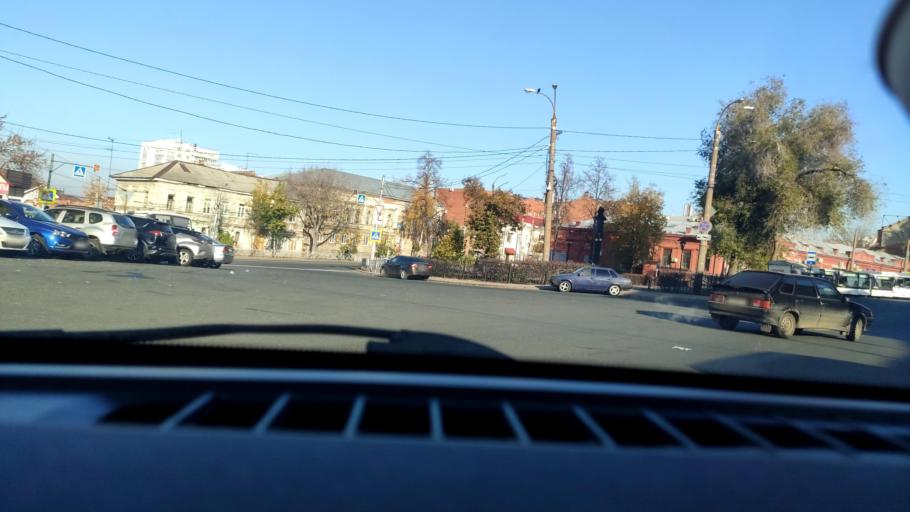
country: RU
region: Samara
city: Rozhdestveno
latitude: 53.1792
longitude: 50.0795
